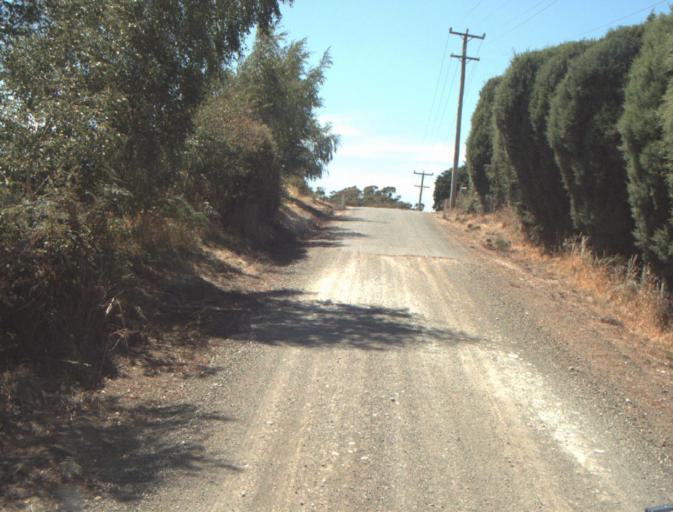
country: AU
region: Tasmania
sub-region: Launceston
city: Mayfield
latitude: -41.2452
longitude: 147.1233
